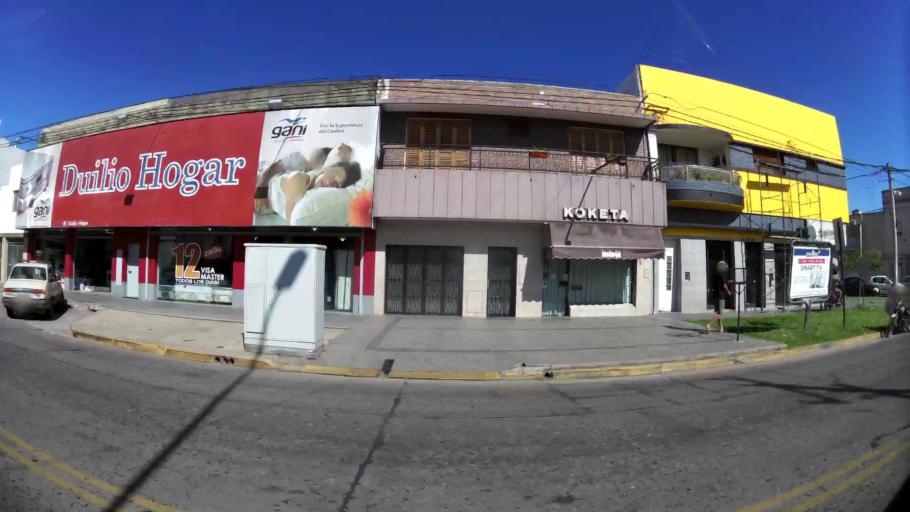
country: AR
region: Santa Fe
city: Santa Fe de la Vera Cruz
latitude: -31.6231
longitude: -60.6878
